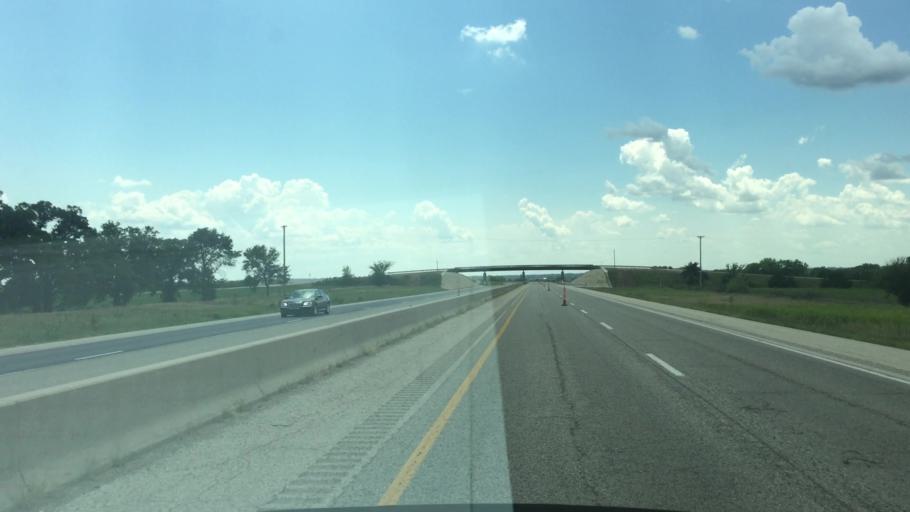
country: US
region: Kansas
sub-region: Shawnee County
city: Auburn
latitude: 38.7989
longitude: -95.9055
